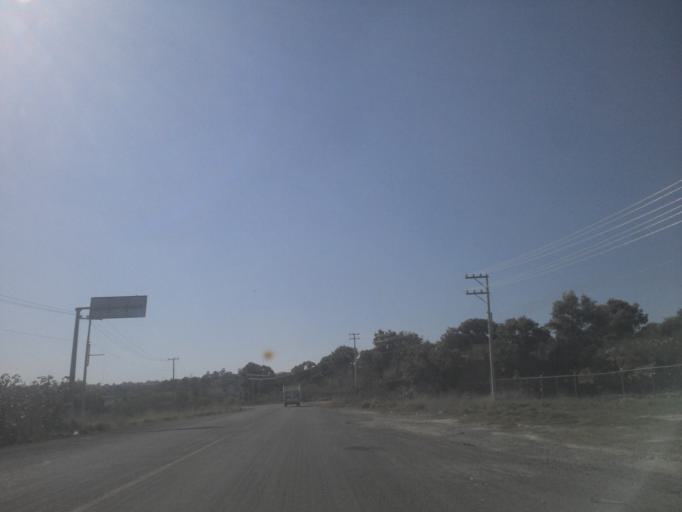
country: MX
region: Jalisco
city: Arandas
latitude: 20.7265
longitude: -102.3288
